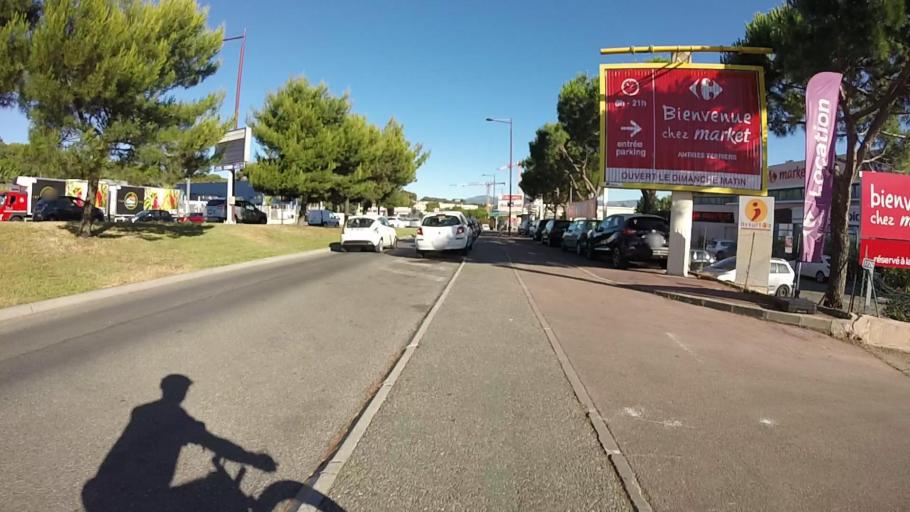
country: FR
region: Provence-Alpes-Cote d'Azur
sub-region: Departement des Alpes-Maritimes
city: Biot
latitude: 43.5978
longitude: 7.0889
